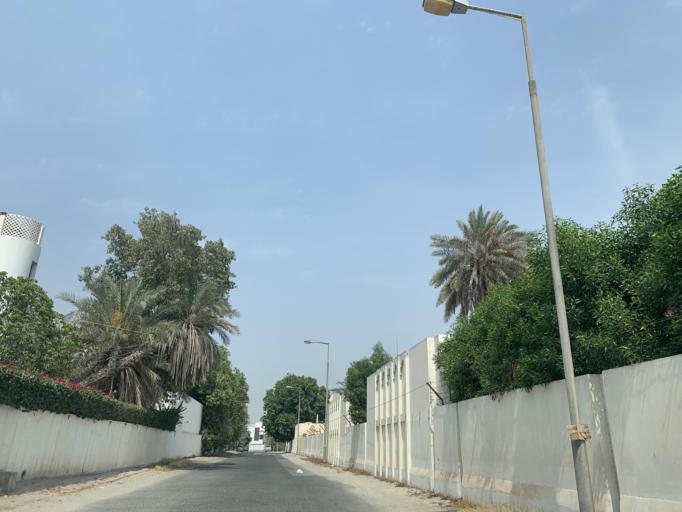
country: BH
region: Manama
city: Jidd Hafs
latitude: 26.2046
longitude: 50.4865
